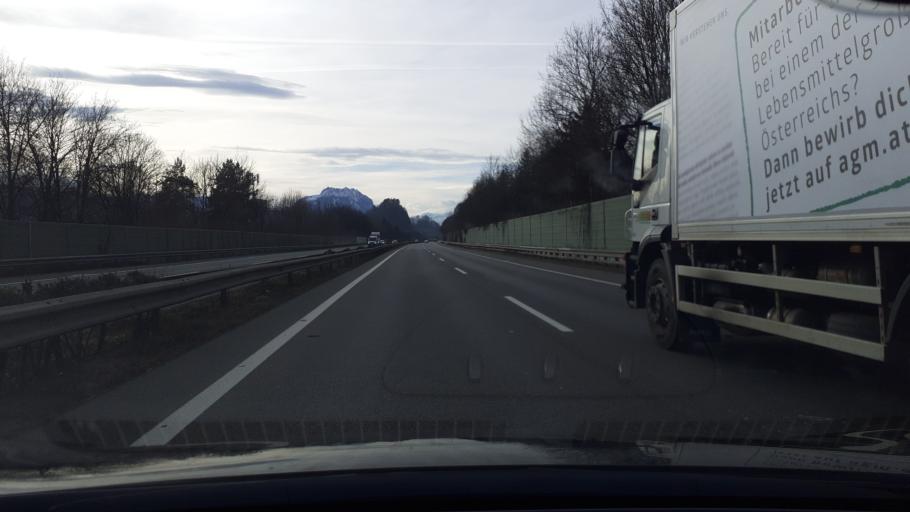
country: AT
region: Vorarlberg
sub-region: Politischer Bezirk Feldkirch
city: Gotzis
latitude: 47.3428
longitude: 9.6341
